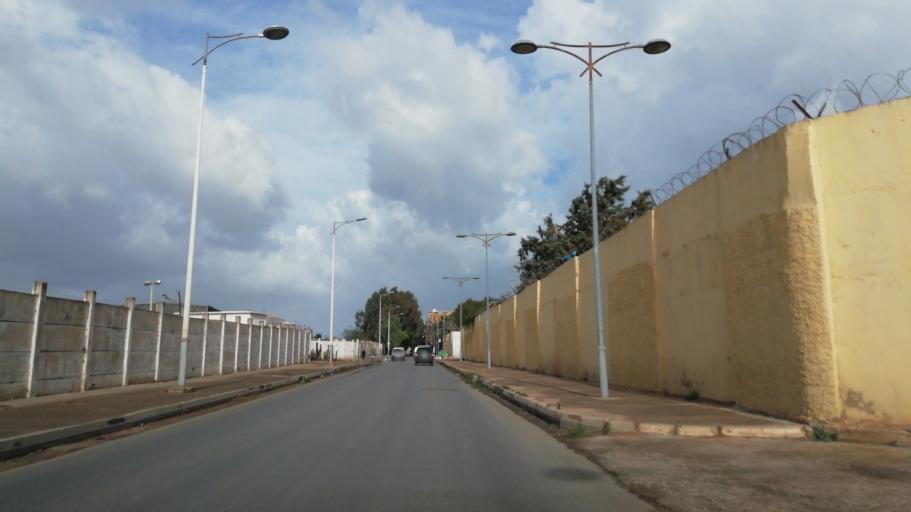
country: DZ
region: Oran
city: Oran
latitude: 35.6807
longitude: -0.6254
